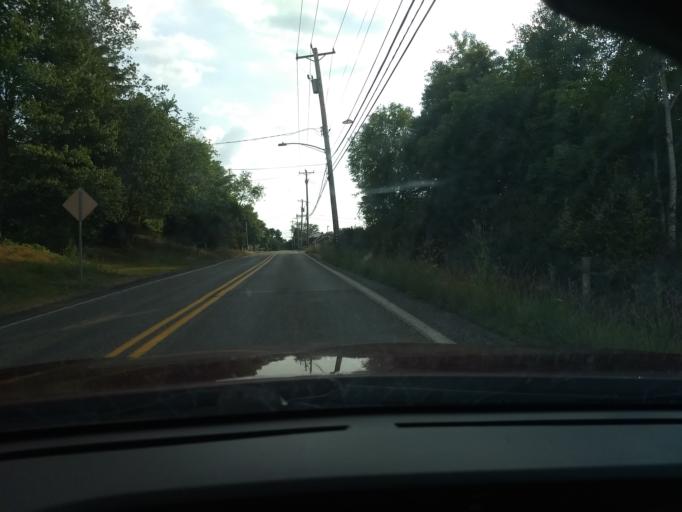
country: US
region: Pennsylvania
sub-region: Allegheny County
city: Curtisville
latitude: 40.6305
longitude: -79.8868
